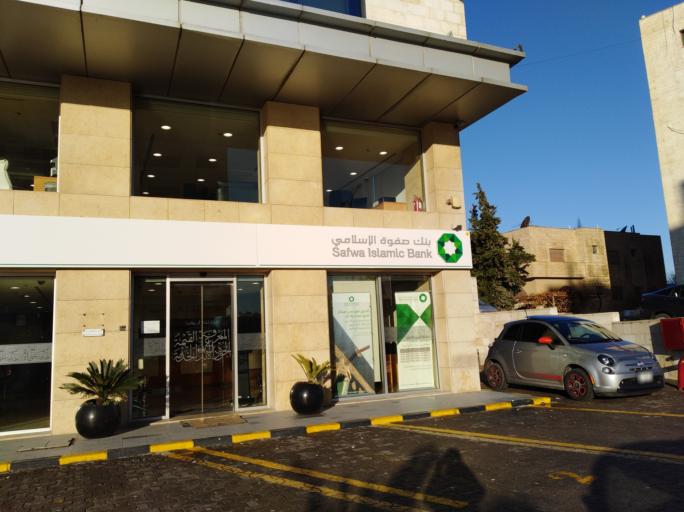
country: JO
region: Amman
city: Al Jubayhah
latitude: 31.9771
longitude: 35.8655
